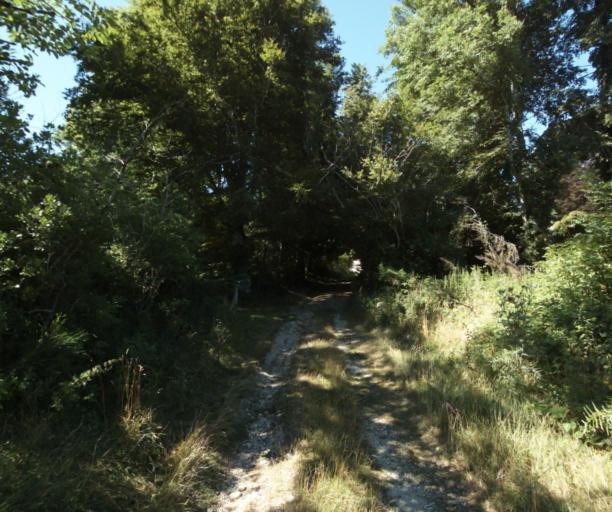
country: FR
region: Midi-Pyrenees
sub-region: Departement du Tarn
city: Dourgne
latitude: 43.4366
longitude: 2.1286
